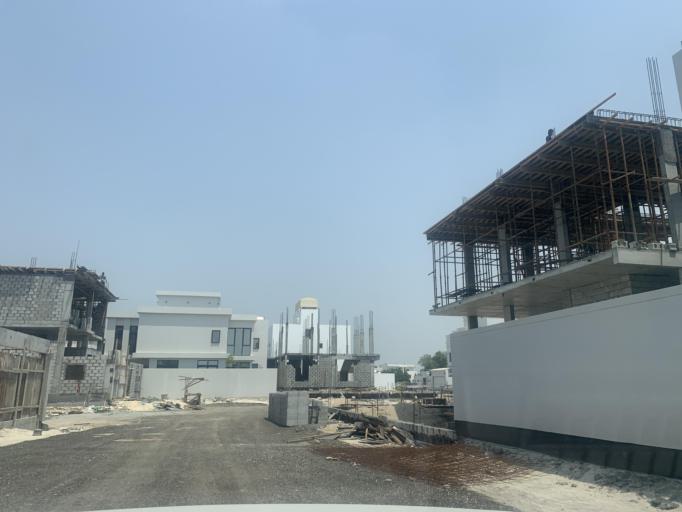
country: BH
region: Central Governorate
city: Madinat Hamad
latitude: 26.1433
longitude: 50.4663
